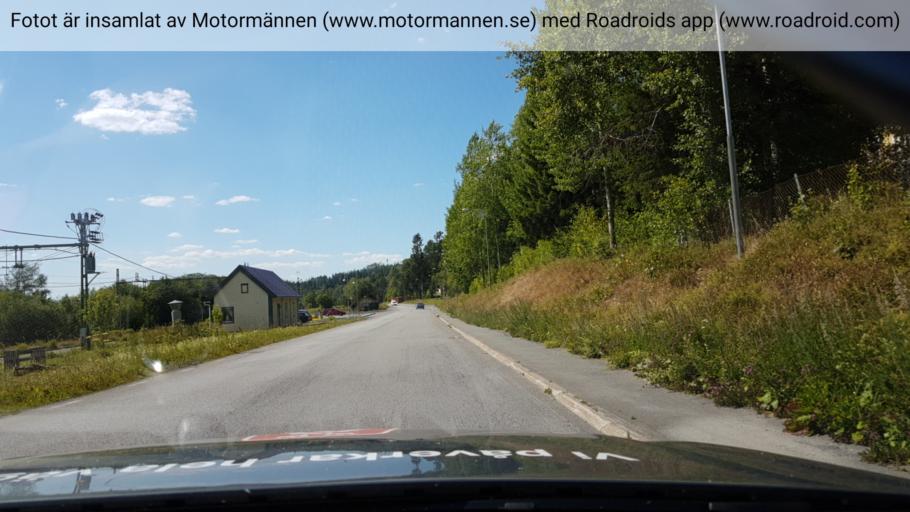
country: SE
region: Jaemtland
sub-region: Are Kommun
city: Jarpen
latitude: 63.3083
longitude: 13.6605
